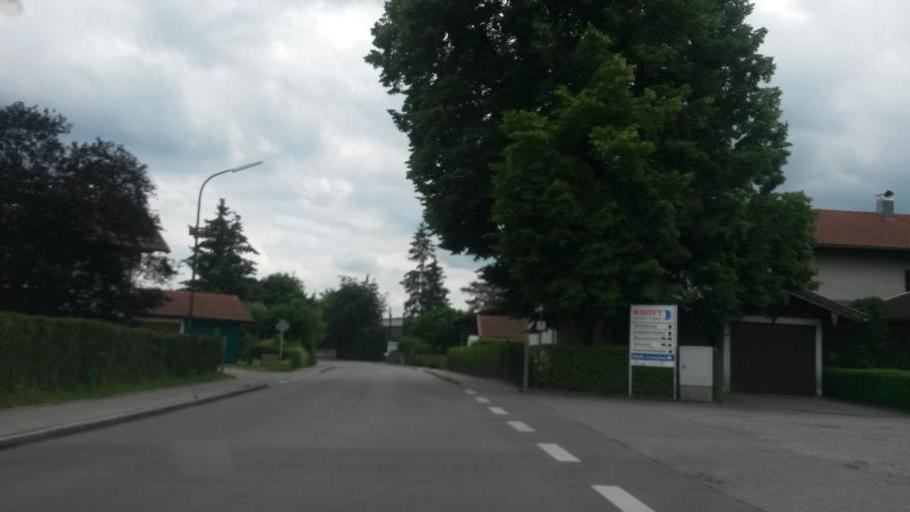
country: DE
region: Bavaria
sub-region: Upper Bavaria
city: Eggstatt
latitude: 47.9304
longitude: 12.3757
